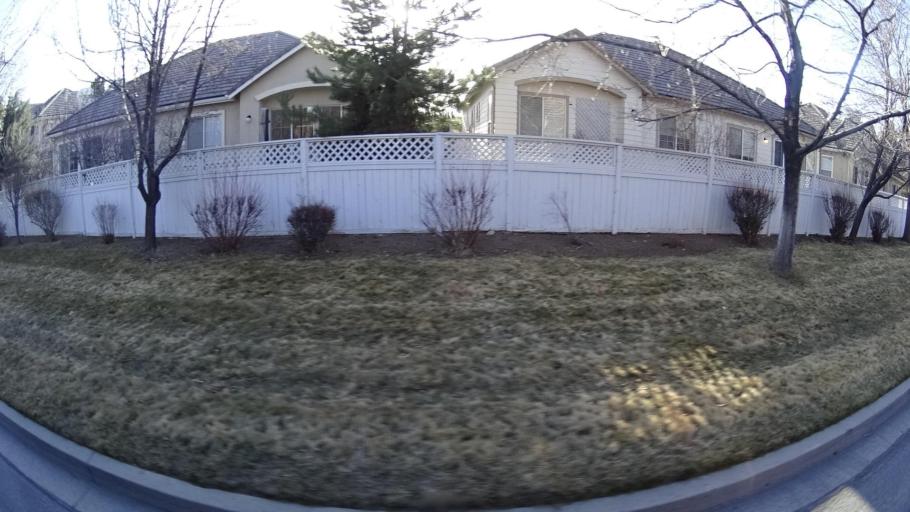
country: US
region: Nevada
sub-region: Washoe County
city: Reno
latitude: 39.5001
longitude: -119.8622
